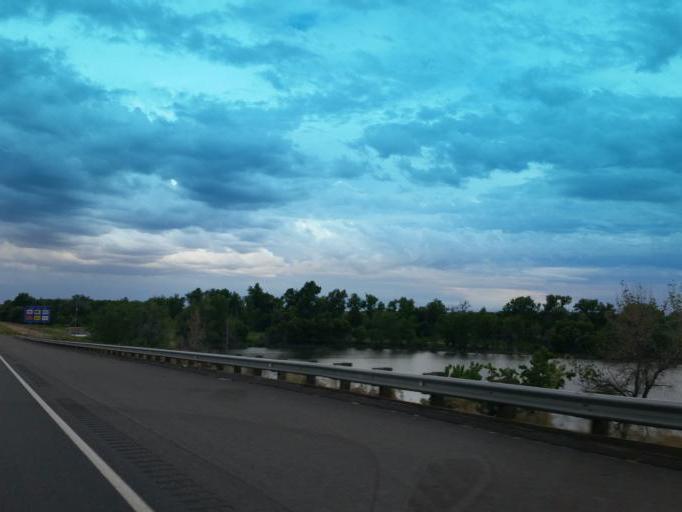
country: US
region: Colorado
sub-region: Larimer County
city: Fort Collins
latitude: 40.5378
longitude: -104.9955
